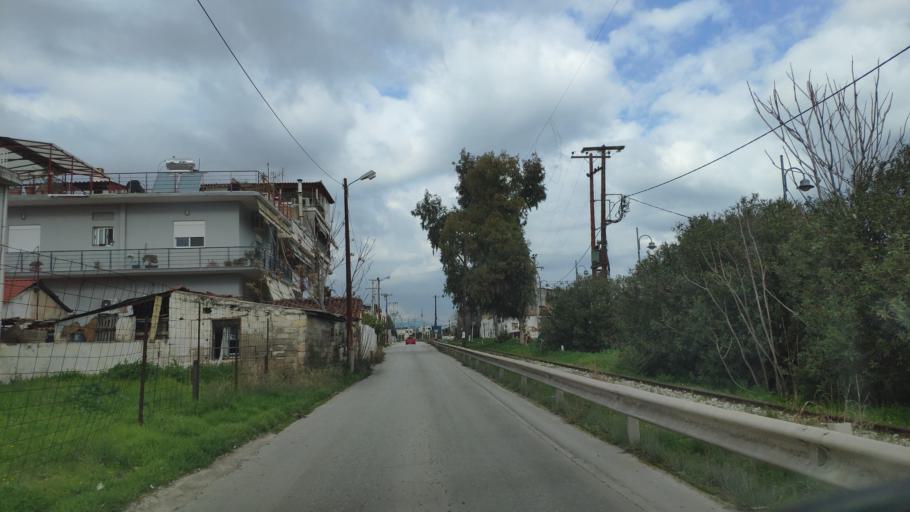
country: GR
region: Peloponnese
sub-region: Nomos Argolidos
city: Argos
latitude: 37.6342
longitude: 22.7357
